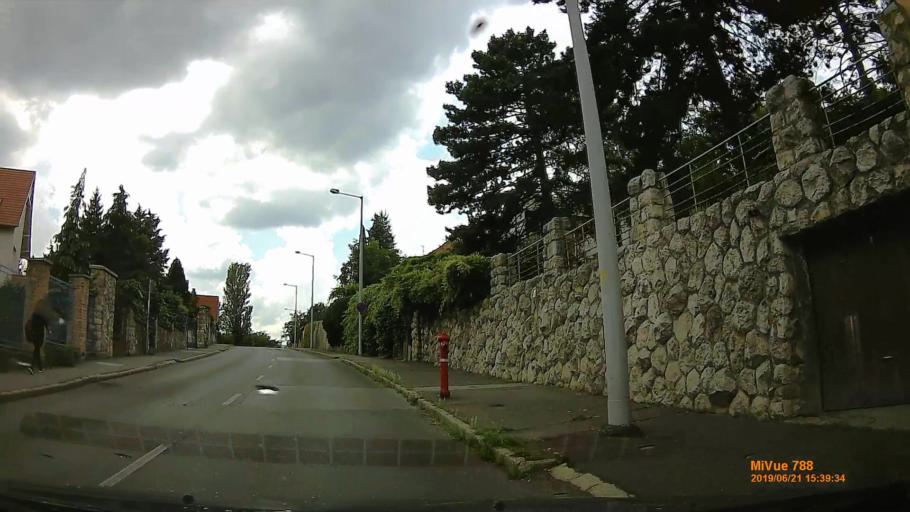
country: HU
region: Baranya
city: Pecs
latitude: 46.0801
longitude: 18.2188
